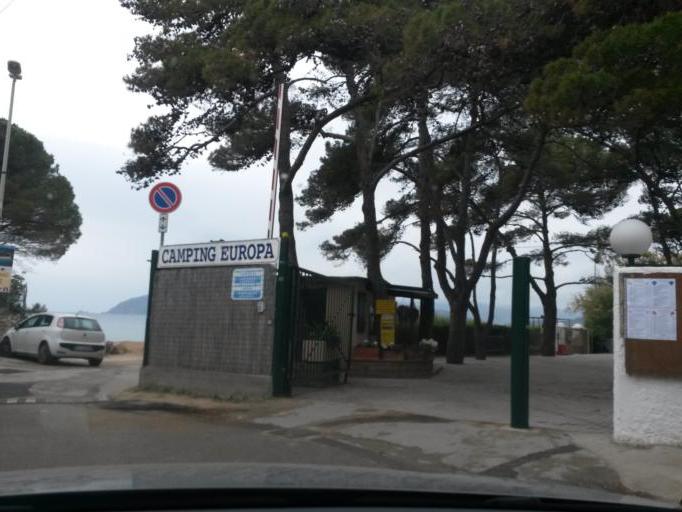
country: IT
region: Tuscany
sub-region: Provincia di Livorno
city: Capoliveri
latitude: 42.7597
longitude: 10.3581
